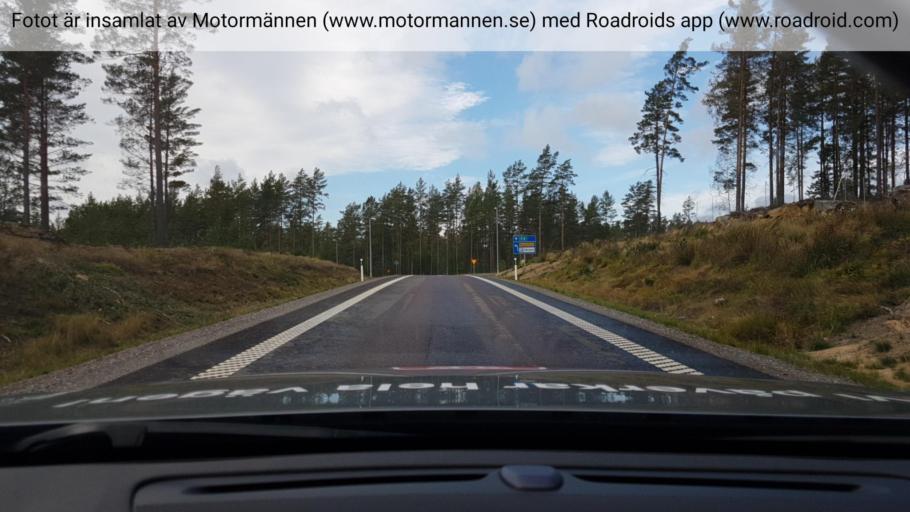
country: SE
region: Vaermland
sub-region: Kils Kommun
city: Kil
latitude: 59.3852
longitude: 13.3375
